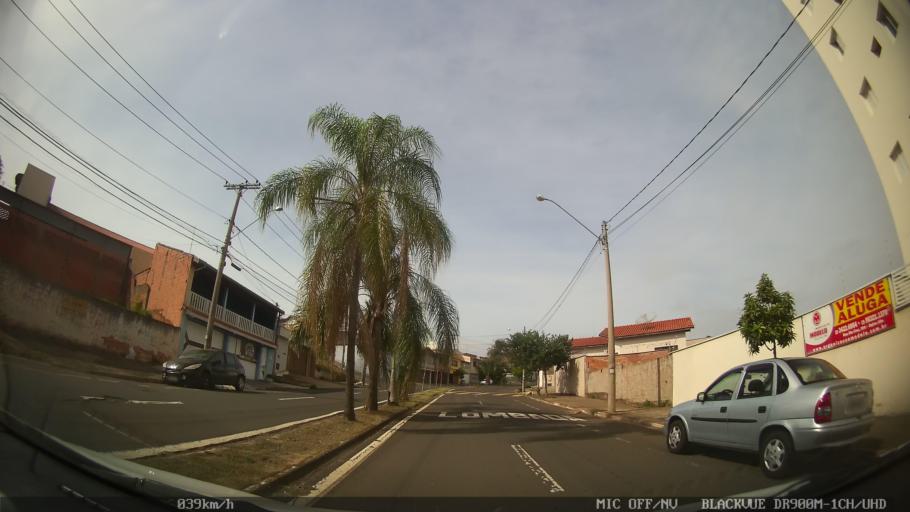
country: BR
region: Sao Paulo
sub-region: Piracicaba
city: Piracicaba
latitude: -22.7325
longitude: -47.6688
